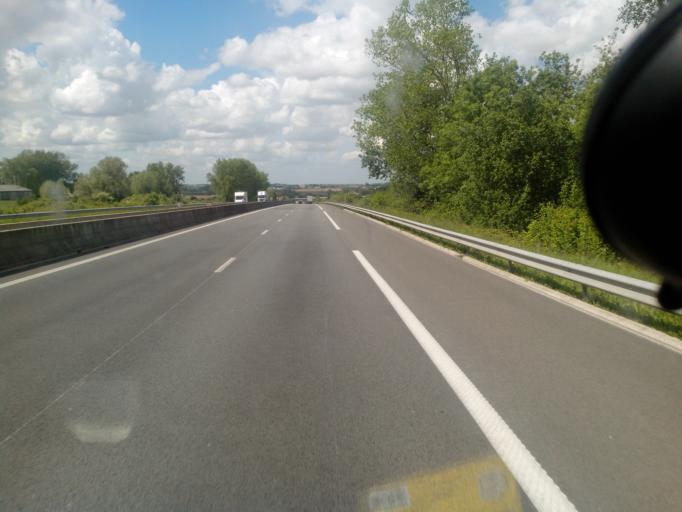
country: FR
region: Nord-Pas-de-Calais
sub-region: Departement du Nord
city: Godewaersvelde
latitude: 50.7841
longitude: 2.6244
